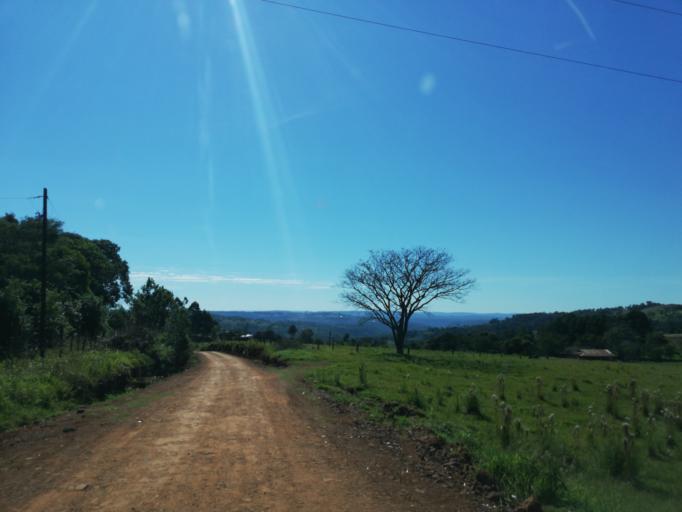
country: AR
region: Misiones
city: Dos de Mayo
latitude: -27.0775
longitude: -54.4023
